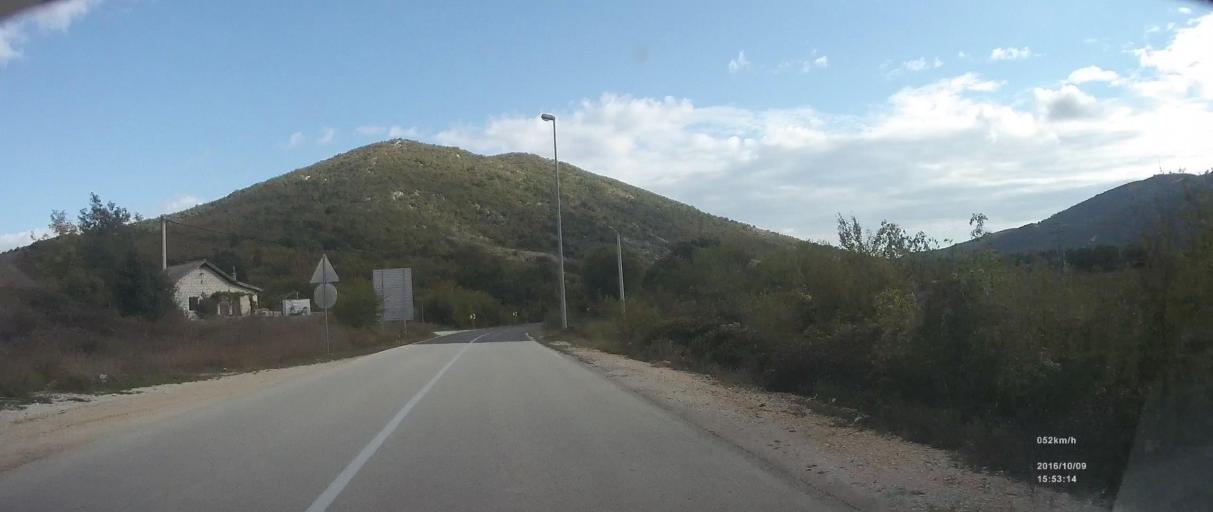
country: HR
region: Splitsko-Dalmatinska
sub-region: Grad Trogir
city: Trogir
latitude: 43.6068
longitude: 16.2242
